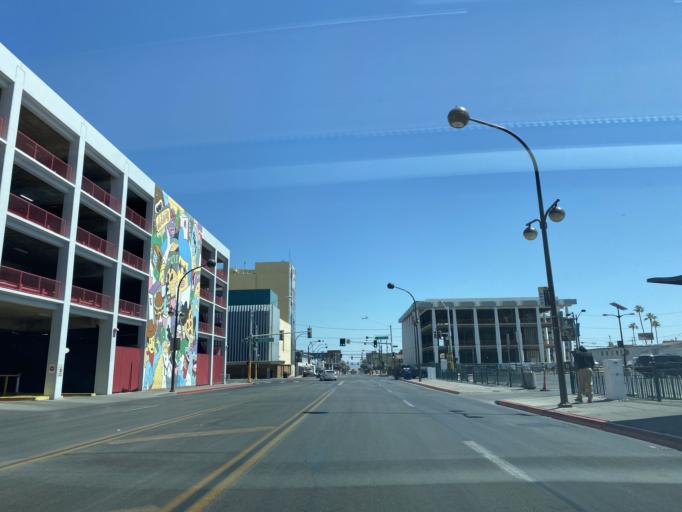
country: US
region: Nevada
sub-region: Clark County
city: Las Vegas
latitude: 36.1684
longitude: -115.1423
